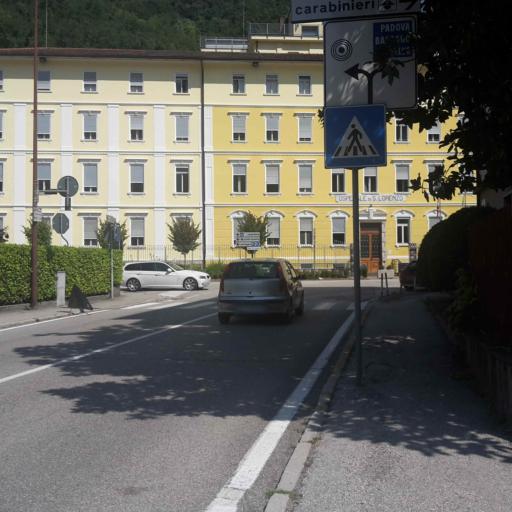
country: IT
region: Trentino-Alto Adige
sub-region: Provincia di Trento
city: Borgo
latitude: 46.0562
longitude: 11.4639
